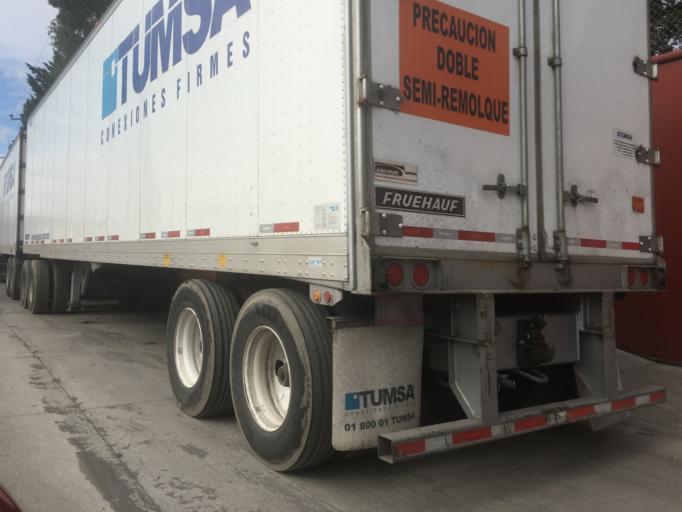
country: MX
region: Mexico
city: Santa Maria Totoltepec
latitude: 19.2908
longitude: -99.5939
